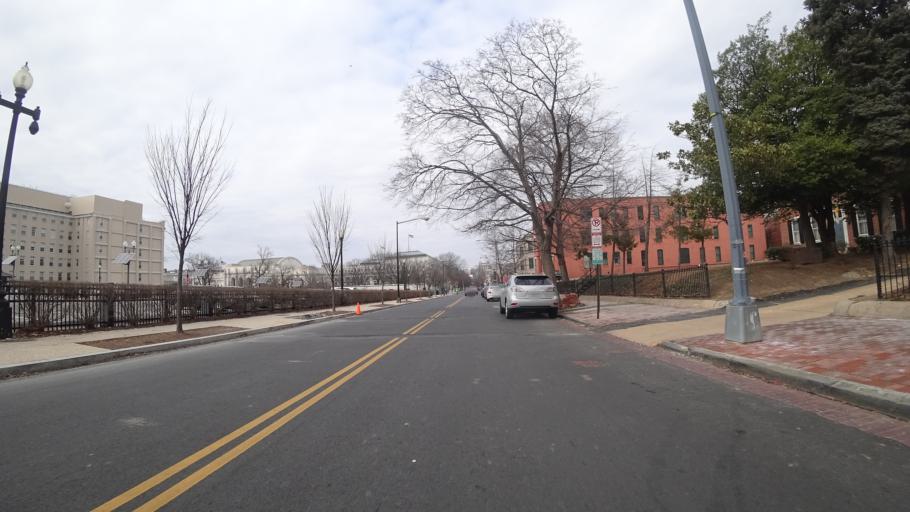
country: US
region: Washington, D.C.
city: Washington, D.C.
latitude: 38.8939
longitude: -77.0035
